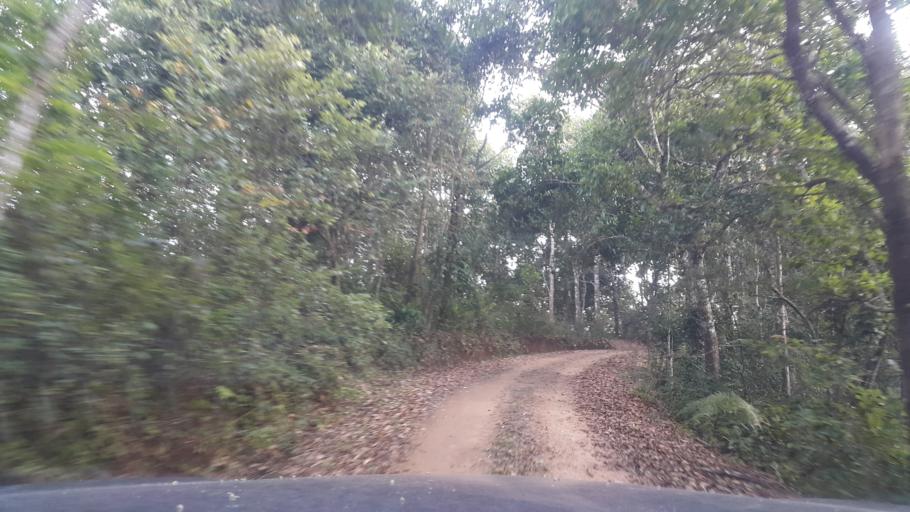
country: TH
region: Chiang Mai
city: Samoeng
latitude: 19.0349
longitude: 98.6533
